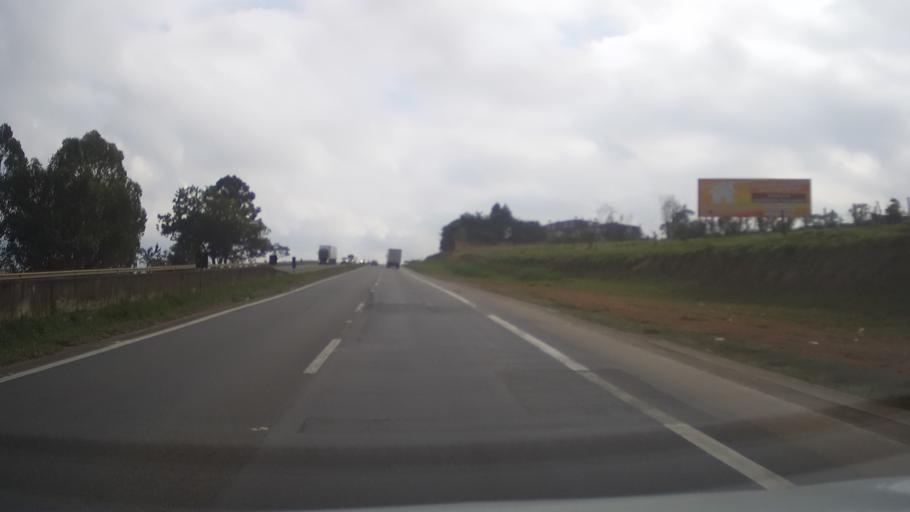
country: BR
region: Minas Gerais
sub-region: Extrema
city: Extrema
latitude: -22.8456
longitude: -46.3317
